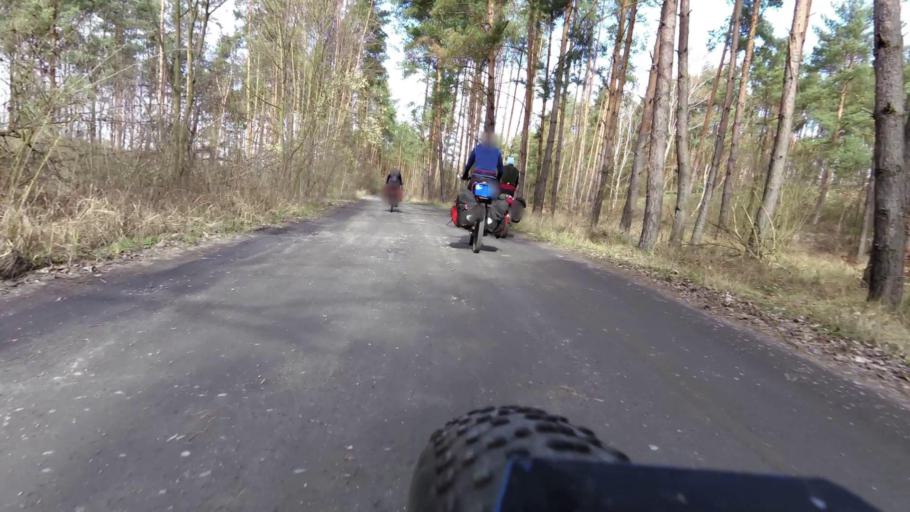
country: PL
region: Lubusz
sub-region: Powiat slubicki
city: Slubice
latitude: 52.3176
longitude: 14.5845
